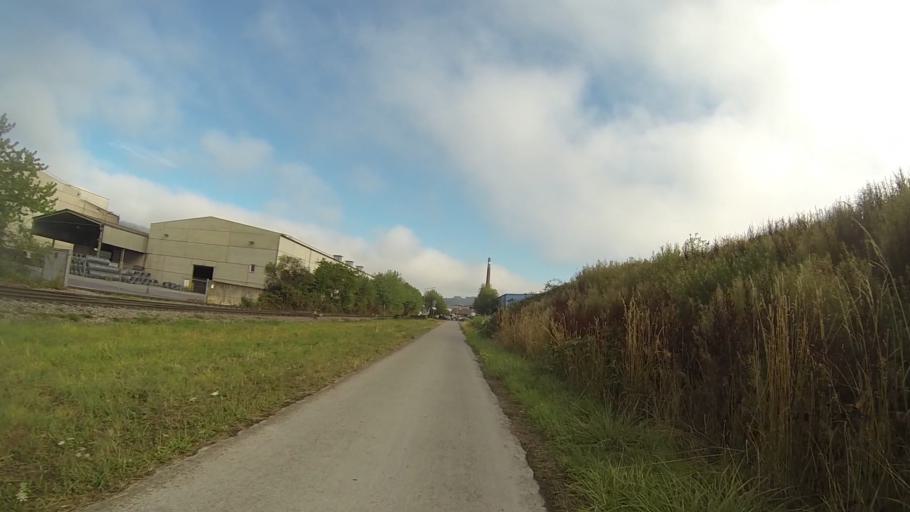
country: DE
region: Rheinland-Pfalz
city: Kenn
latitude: 49.7909
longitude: 6.6945
